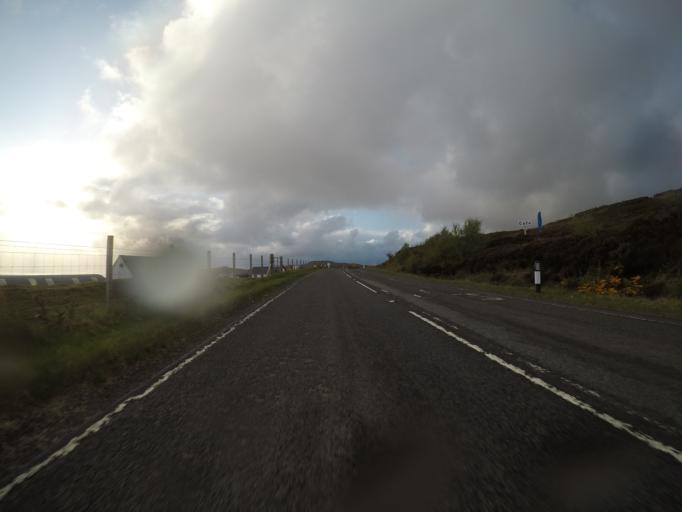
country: GB
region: Scotland
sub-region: Highland
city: Portree
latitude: 57.5728
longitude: -6.3646
